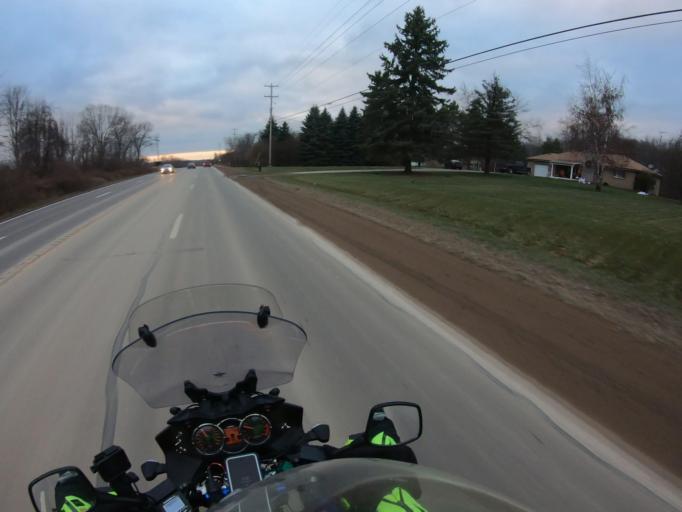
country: US
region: Michigan
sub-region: Genesee County
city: Grand Blanc
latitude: 42.8624
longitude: -83.5822
